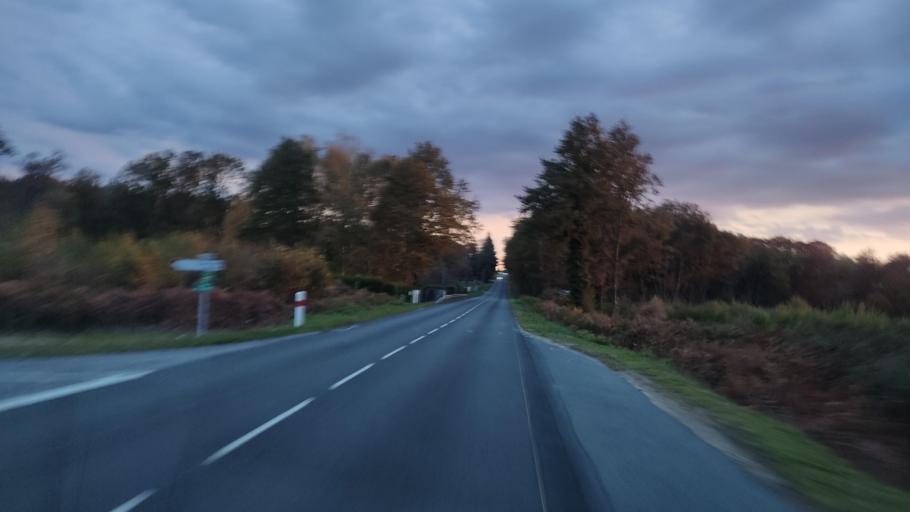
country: FR
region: Limousin
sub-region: Departement de la Haute-Vienne
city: Rilhac-Rancon
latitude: 45.9308
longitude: 1.3469
